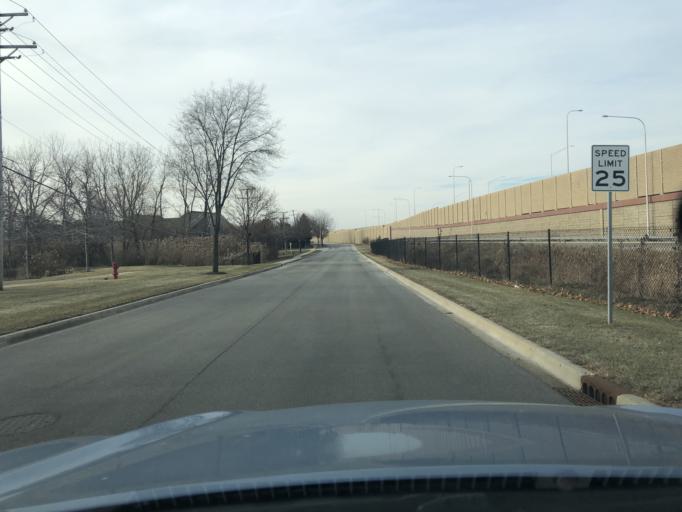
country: US
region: Illinois
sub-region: DuPage County
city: Itasca
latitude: 41.9831
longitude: -88.0146
